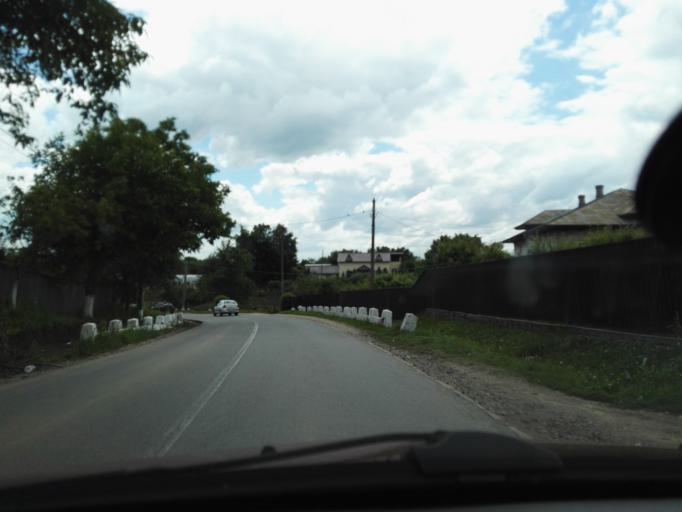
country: RO
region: Giurgiu
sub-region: Comuna Adunatii-Copaceni
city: Adunatii-Copaceni
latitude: 44.2608
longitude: 26.0576
